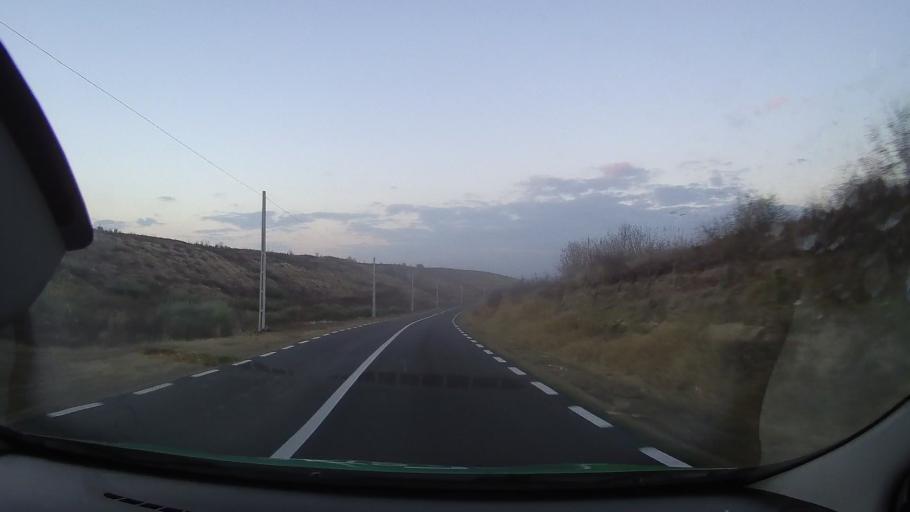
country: RO
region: Constanta
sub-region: Comuna Oltina
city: Oltina
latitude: 44.1374
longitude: 27.6658
